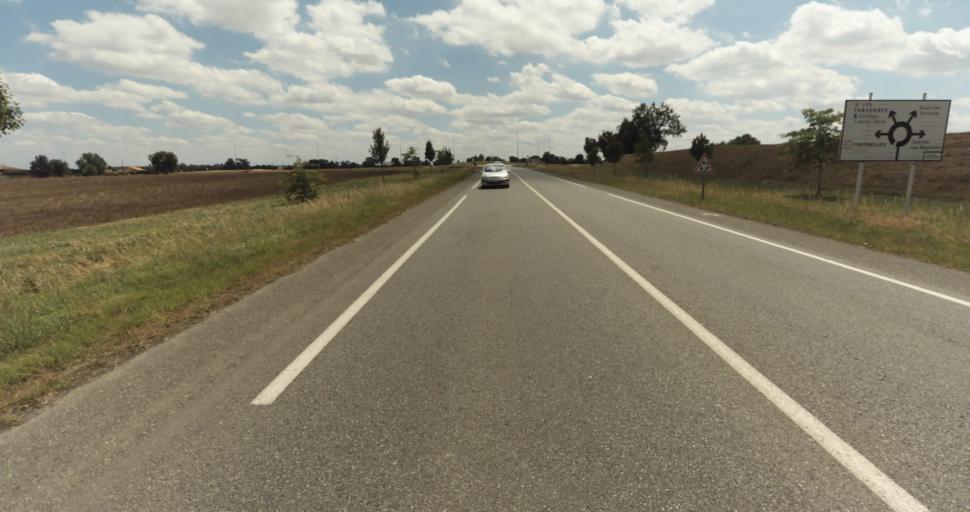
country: FR
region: Midi-Pyrenees
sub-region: Departement de la Haute-Garonne
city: Fontenilles
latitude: 43.5547
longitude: 1.1794
